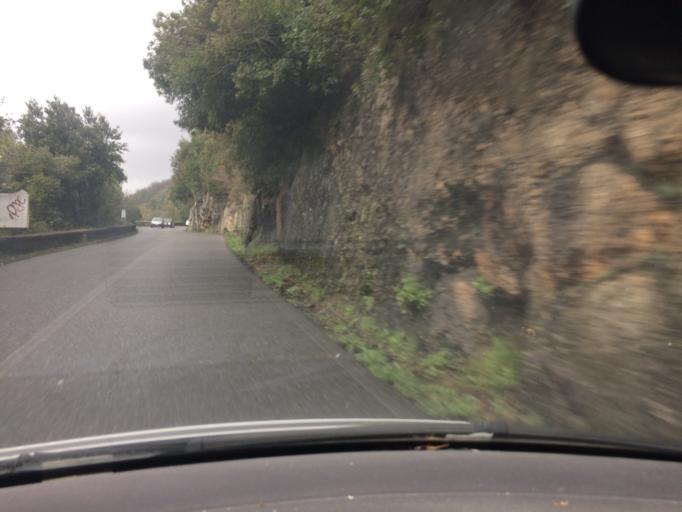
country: IT
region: Tuscany
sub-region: Provincia di Massa-Carrara
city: Massa
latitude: 44.0609
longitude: 10.1193
